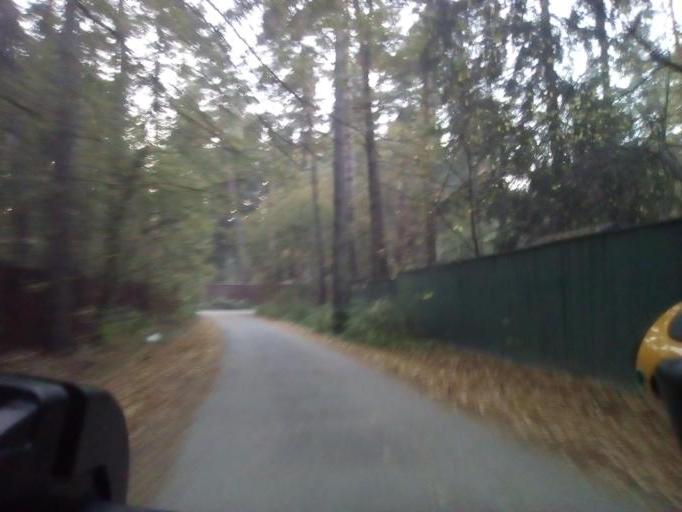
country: RU
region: Moskovskaya
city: Kratovo
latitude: 55.6041
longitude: 38.1756
